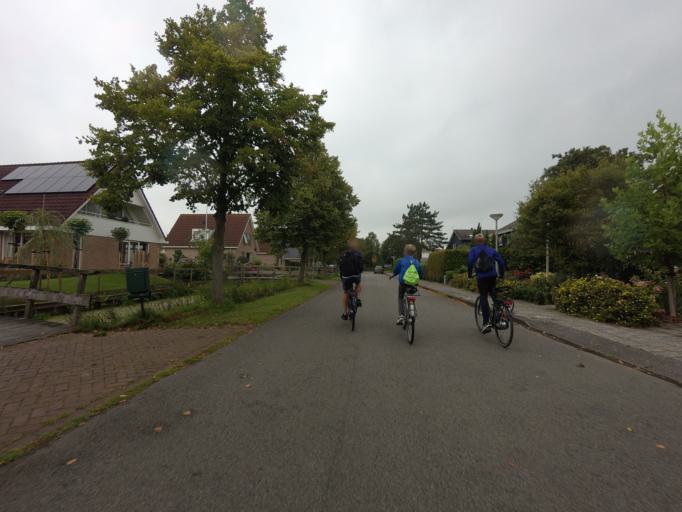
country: NL
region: Friesland
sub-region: Sudwest Fryslan
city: Workum
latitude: 52.9813
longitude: 5.4553
